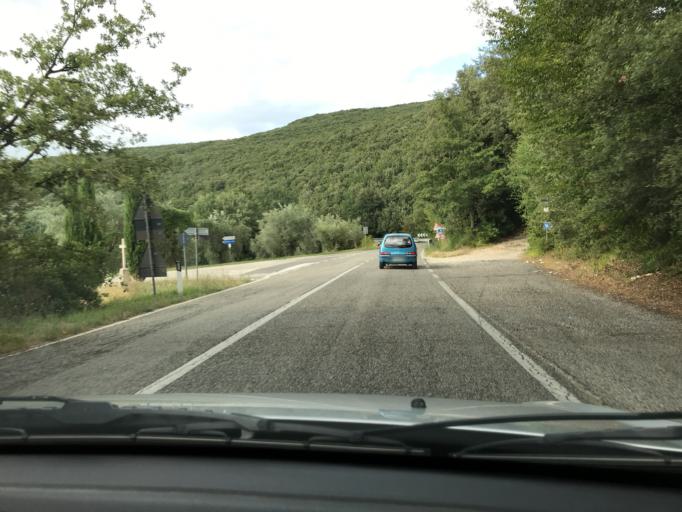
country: IT
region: Umbria
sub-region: Provincia di Terni
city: Guardea
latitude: 42.6368
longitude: 12.2916
